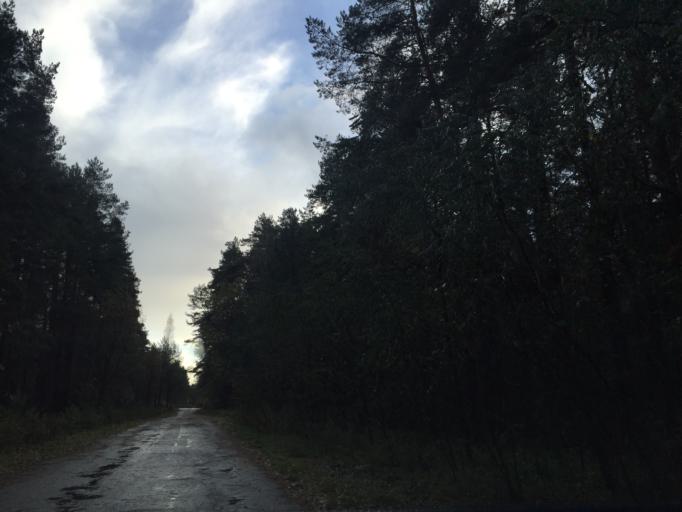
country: LV
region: Riga
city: Bergi
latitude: 57.0170
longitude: 24.3130
